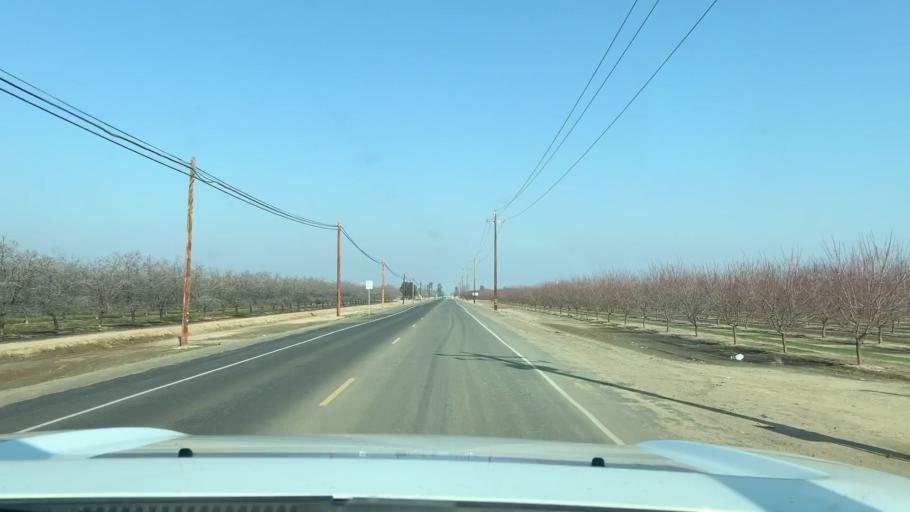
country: US
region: California
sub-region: Kern County
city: Shafter
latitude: 35.4820
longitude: -119.2785
